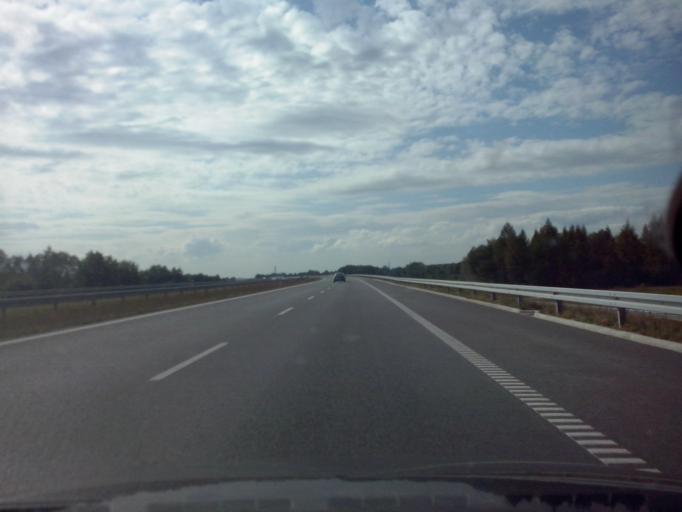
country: PL
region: Lesser Poland Voivodeship
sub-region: Powiat tarnowski
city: Jodlowka-Walki
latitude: 50.0789
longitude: 21.1098
